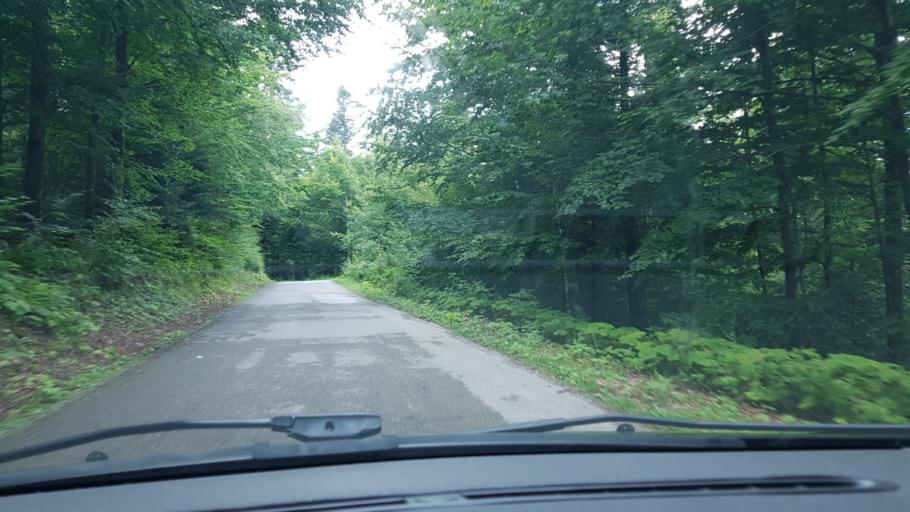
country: HR
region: Primorsko-Goranska
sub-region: Grad Delnice
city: Delnice
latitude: 45.3761
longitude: 14.7066
